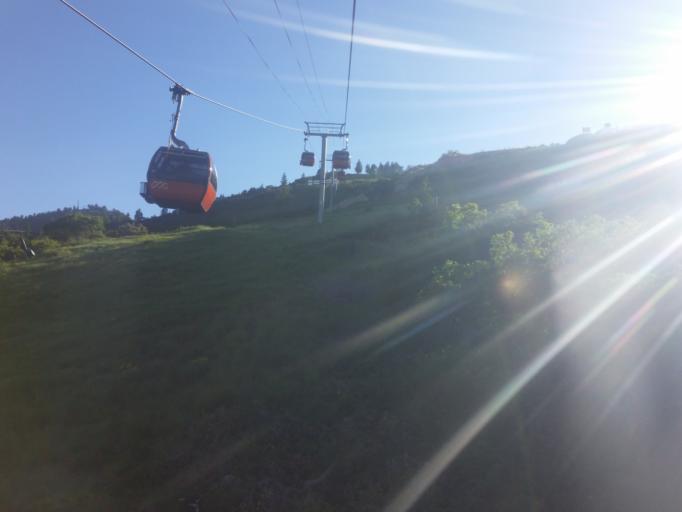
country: US
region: Utah
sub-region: Summit County
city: Snyderville
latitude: 40.6850
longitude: -111.5613
